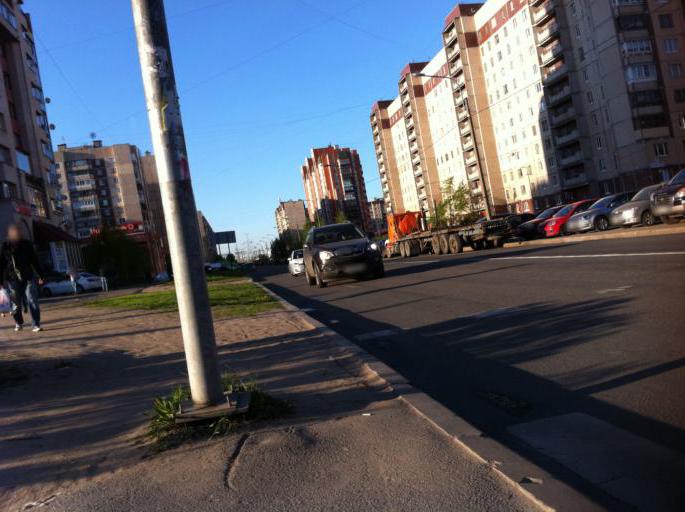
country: RU
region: St.-Petersburg
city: Uritsk
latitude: 59.8549
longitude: 30.2092
